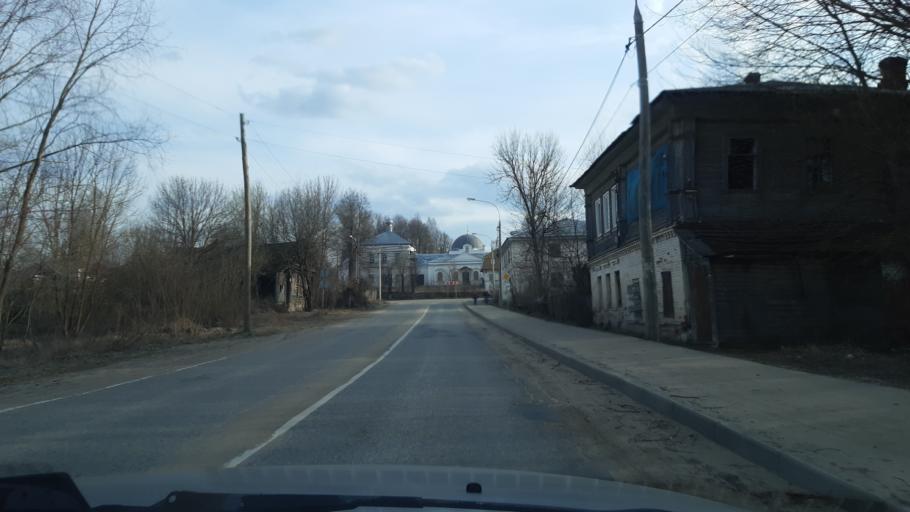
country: RU
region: Vladimir
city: Nikologory
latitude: 56.1424
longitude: 41.9935
